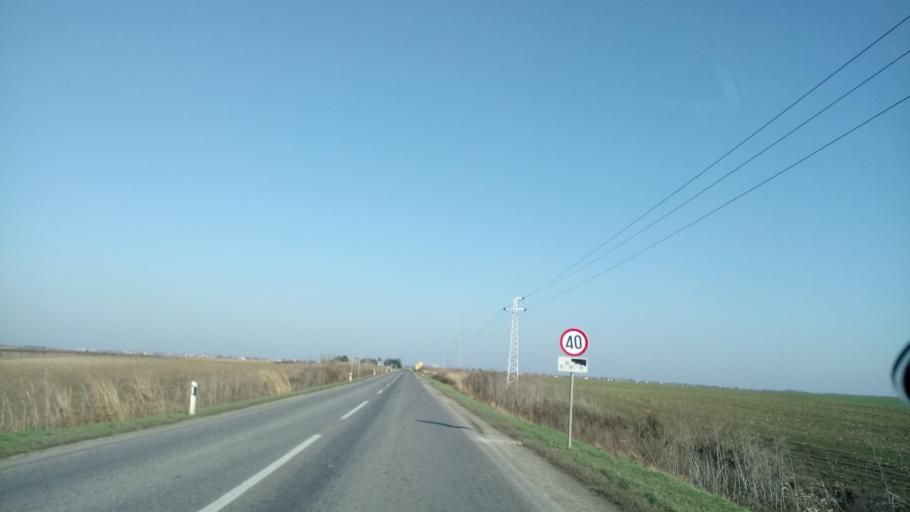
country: RS
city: Ljukovo
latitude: 45.0244
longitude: 20.0418
